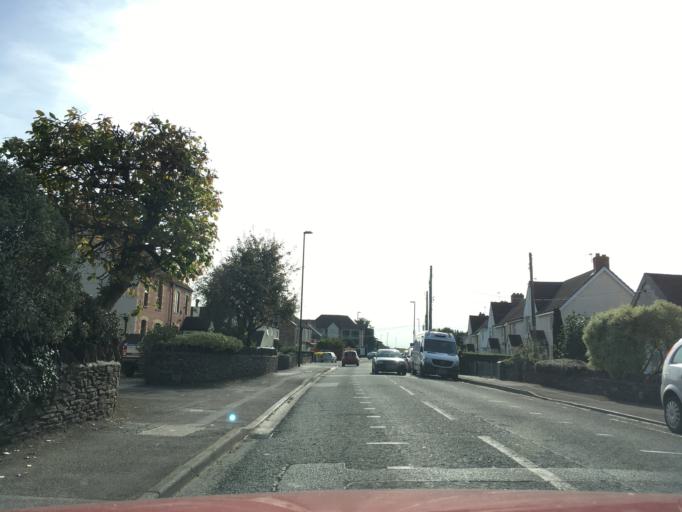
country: GB
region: England
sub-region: South Gloucestershire
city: Yate
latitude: 51.5381
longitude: -2.4215
